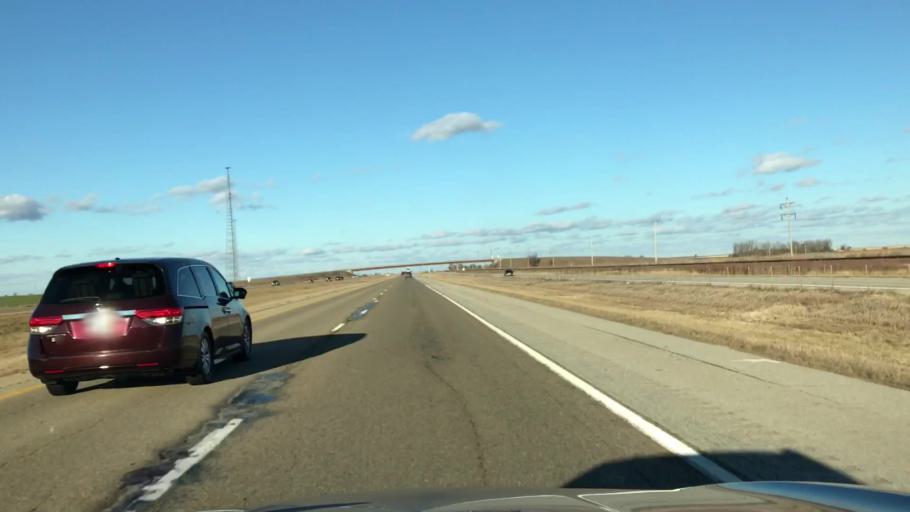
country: US
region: Illinois
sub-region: McLean County
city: Lexington
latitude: 40.6762
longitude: -88.7641
